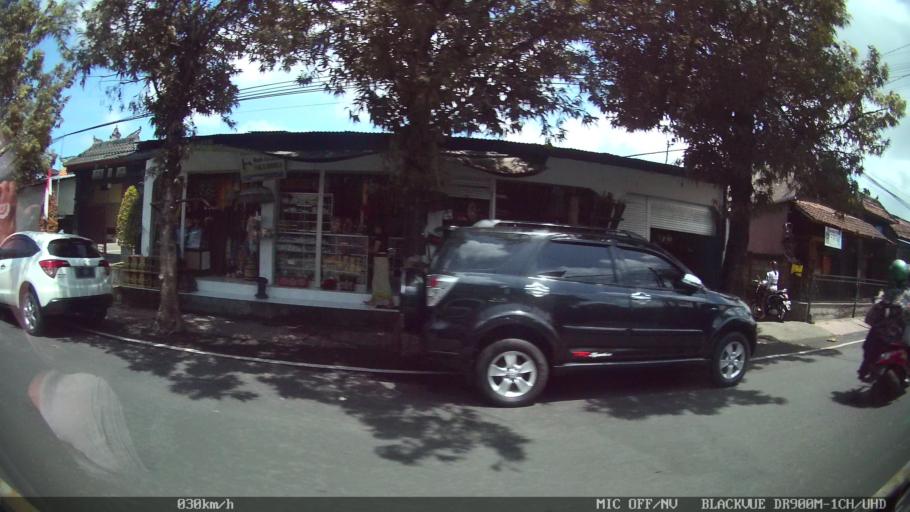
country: ID
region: Bali
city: Banjar Pasekan
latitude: -8.6014
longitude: 115.2831
